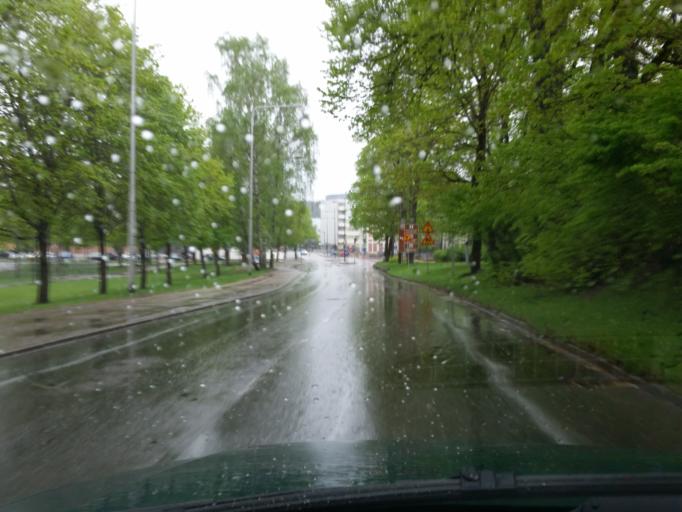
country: FI
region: Uusimaa
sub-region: Helsinki
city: Lohja
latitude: 60.2541
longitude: 24.0642
